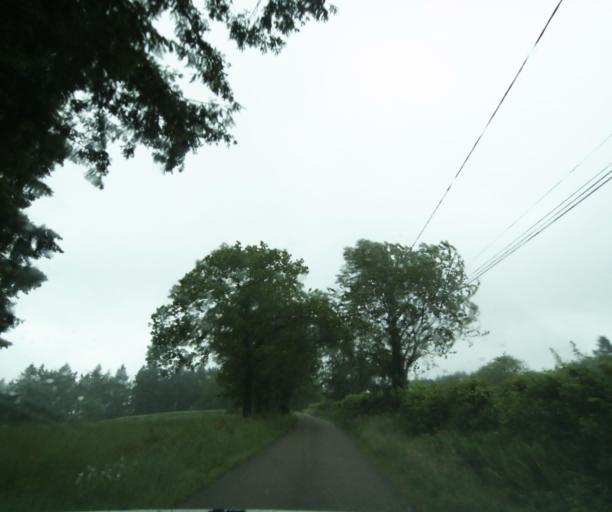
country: FR
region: Bourgogne
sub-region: Departement de Saone-et-Loire
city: Charolles
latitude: 46.3786
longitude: 4.3424
